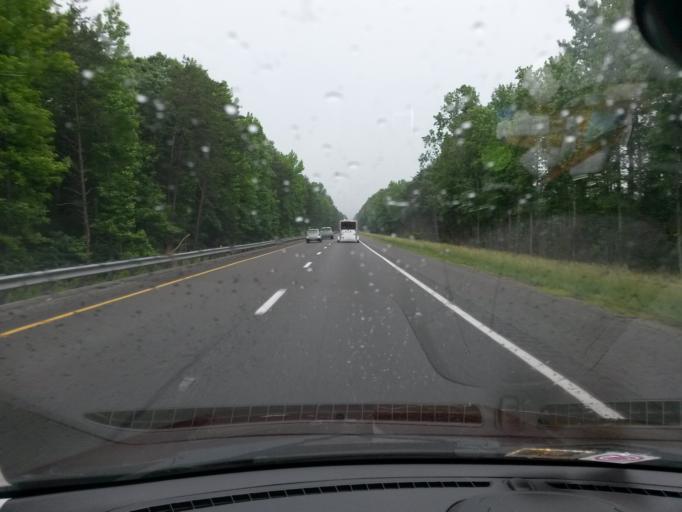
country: US
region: Virginia
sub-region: Louisa County
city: Louisa
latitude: 37.8563
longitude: -77.9958
